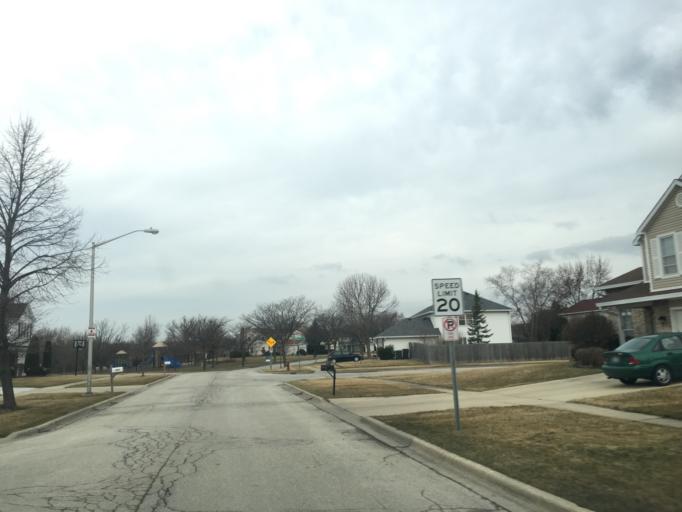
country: US
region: Illinois
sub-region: Cook County
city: Schaumburg
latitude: 42.0382
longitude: -88.1103
